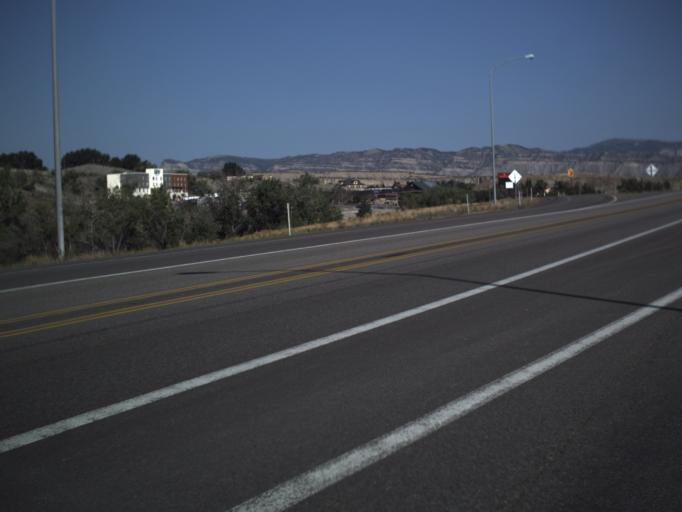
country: US
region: Utah
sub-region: Carbon County
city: Price
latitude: 39.5975
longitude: -110.8245
